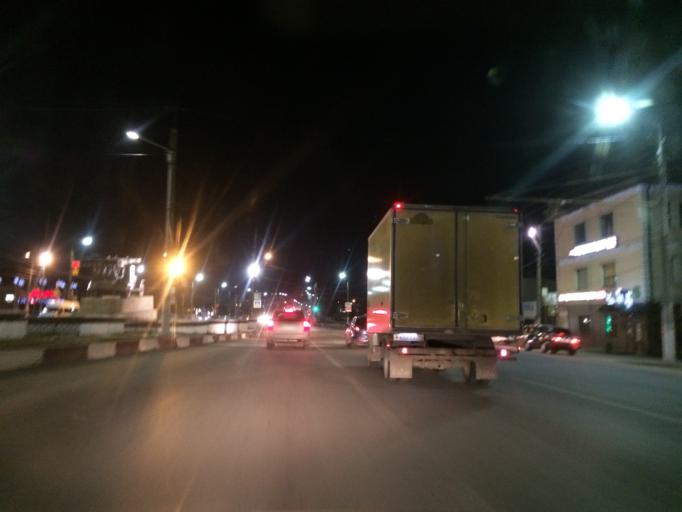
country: RU
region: Tula
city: Tula
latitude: 54.1999
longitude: 37.6360
